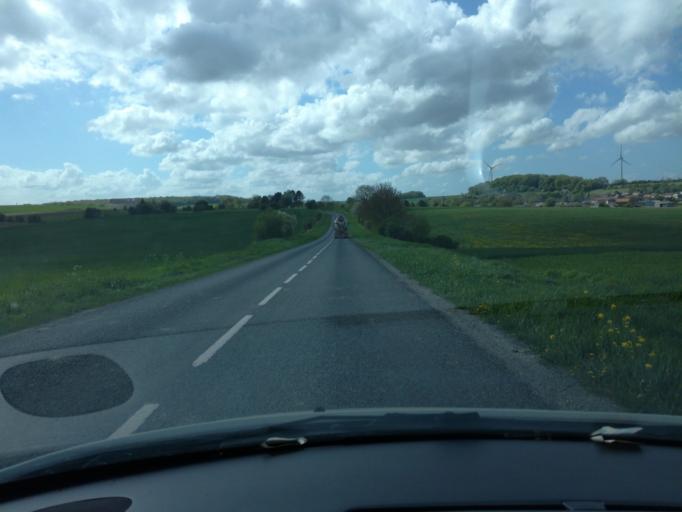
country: FR
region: Picardie
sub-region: Departement de la Somme
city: Picquigny
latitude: 49.8908
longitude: 2.1228
